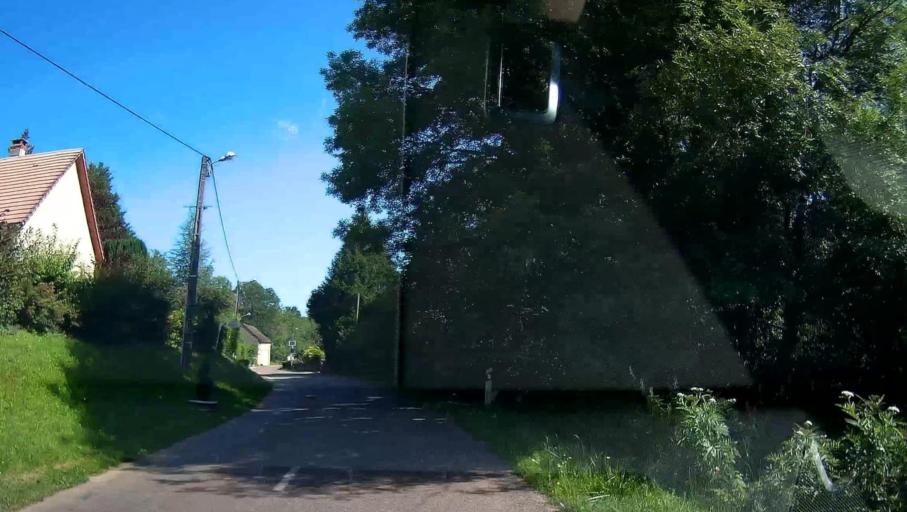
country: FR
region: Bourgogne
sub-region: Departement de la Cote-d'Or
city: Nolay
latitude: 46.9602
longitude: 4.6414
